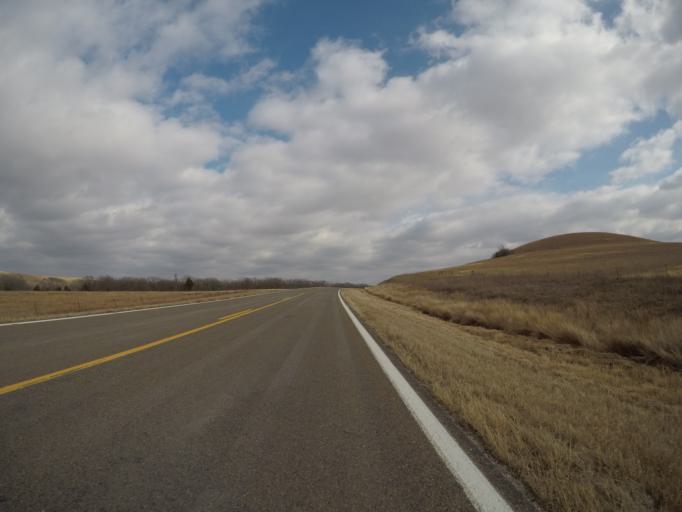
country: US
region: Kansas
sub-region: Wabaunsee County
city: Alma
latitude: 38.8713
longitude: -96.3546
